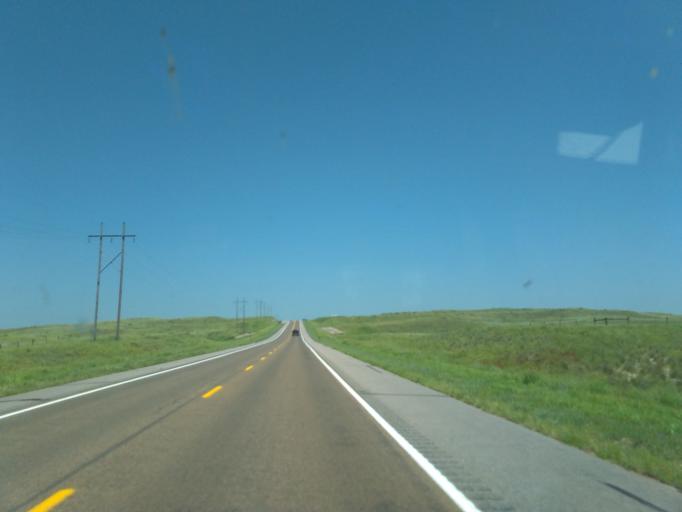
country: US
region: Nebraska
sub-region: Lincoln County
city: North Platte
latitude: 40.8681
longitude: -100.7540
